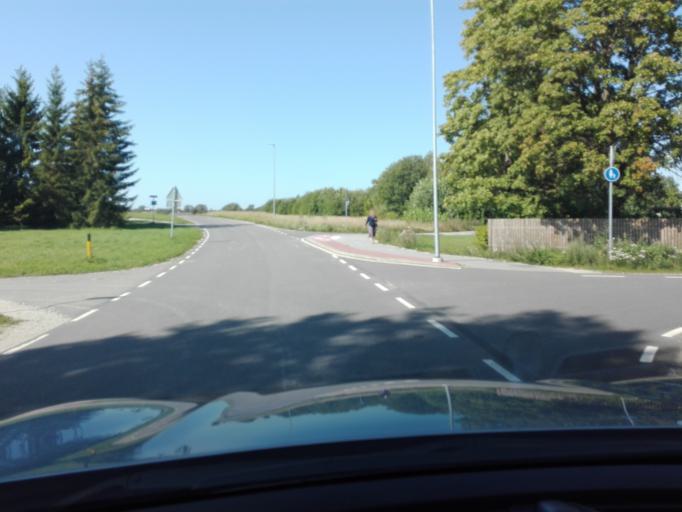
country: EE
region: Raplamaa
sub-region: Rapla vald
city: Rapla
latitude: 59.0241
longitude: 24.7624
